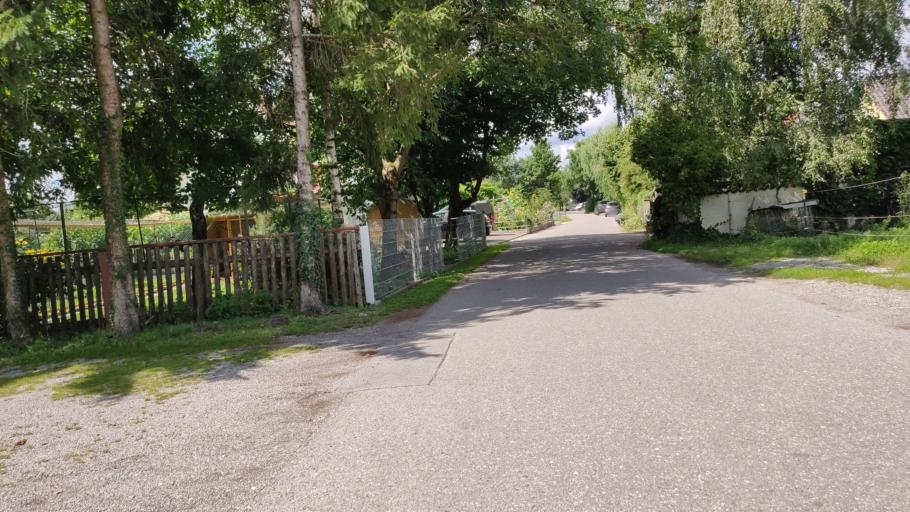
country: DE
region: Bavaria
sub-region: Swabia
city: Konigsbrunn
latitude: 48.2483
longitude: 10.8963
